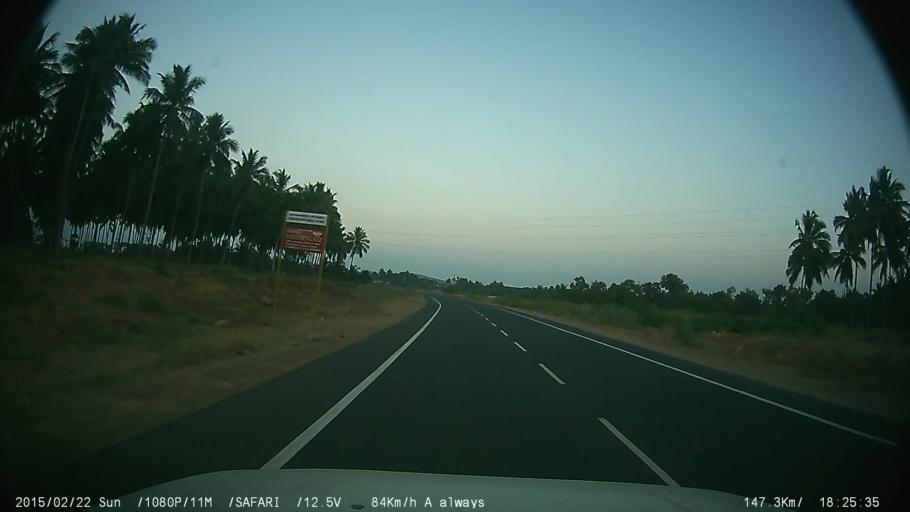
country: IN
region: Tamil Nadu
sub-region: Theni
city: Teni
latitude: 9.9577
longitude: 77.4339
